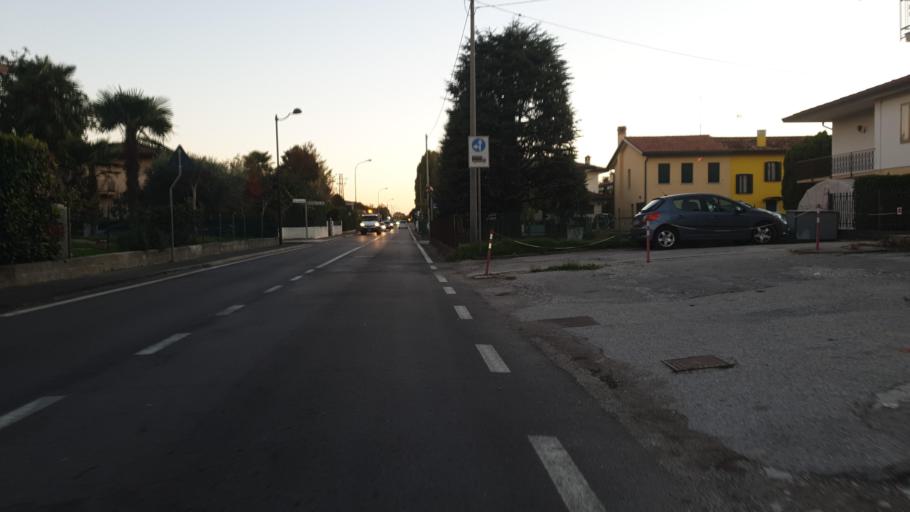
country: IT
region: Veneto
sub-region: Provincia di Venezia
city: Arino
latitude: 45.4377
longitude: 12.0508
